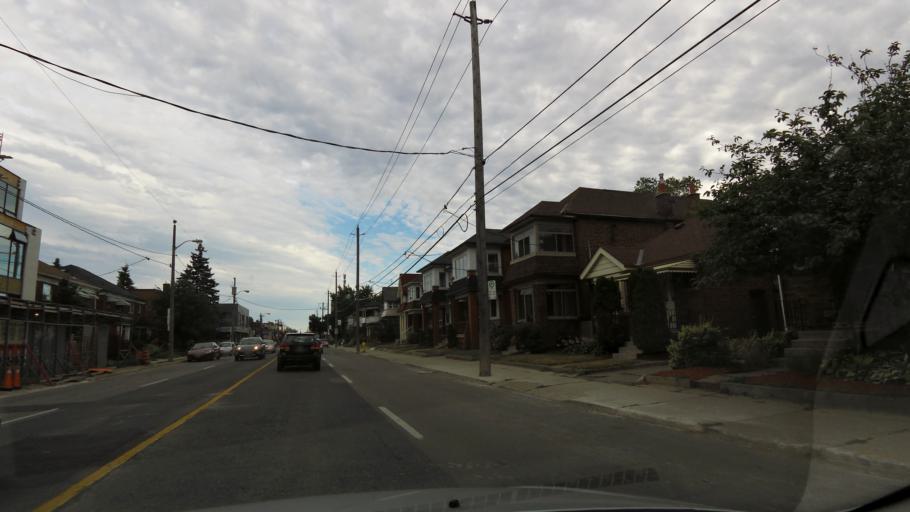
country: CA
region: Ontario
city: Etobicoke
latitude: 43.6599
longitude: -79.4888
